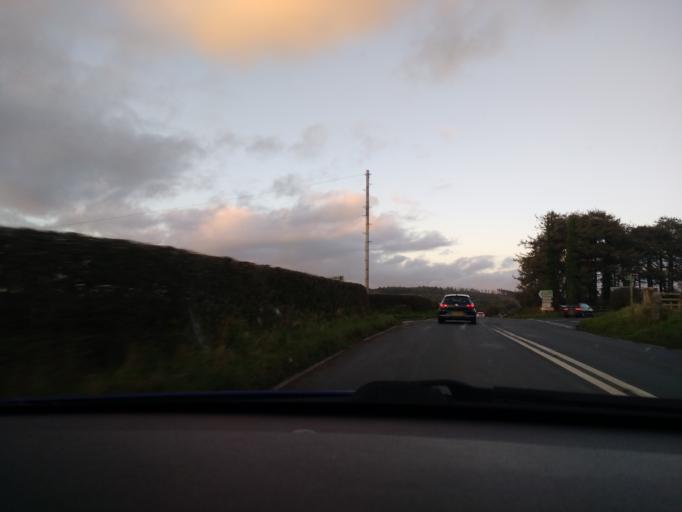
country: GB
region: England
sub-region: Lancashire
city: Caton
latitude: 54.1040
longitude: -2.6451
